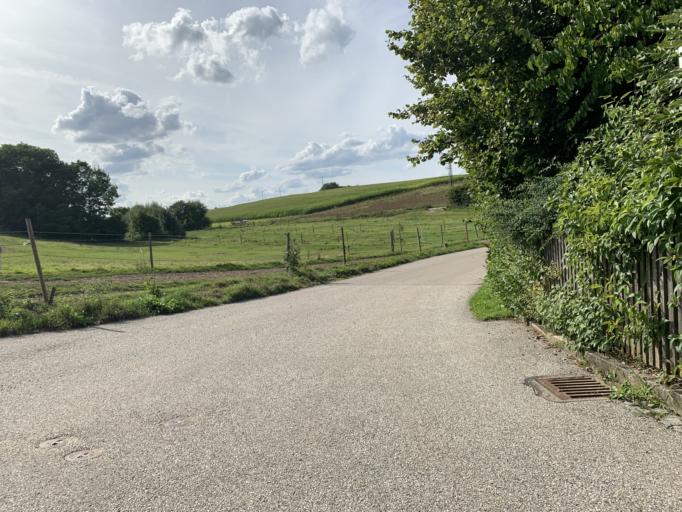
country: DE
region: Bavaria
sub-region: Upper Bavaria
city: Freising
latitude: 48.4278
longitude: 11.7487
